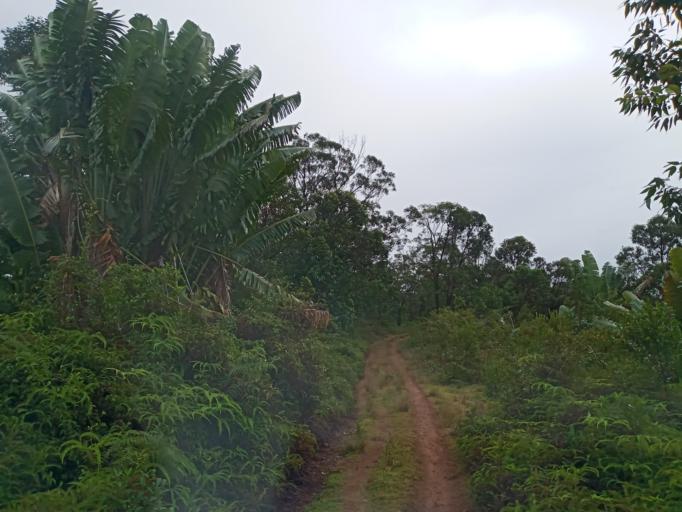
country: MG
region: Atsimo-Atsinanana
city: Vohipaho
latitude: -24.0028
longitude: 47.4042
